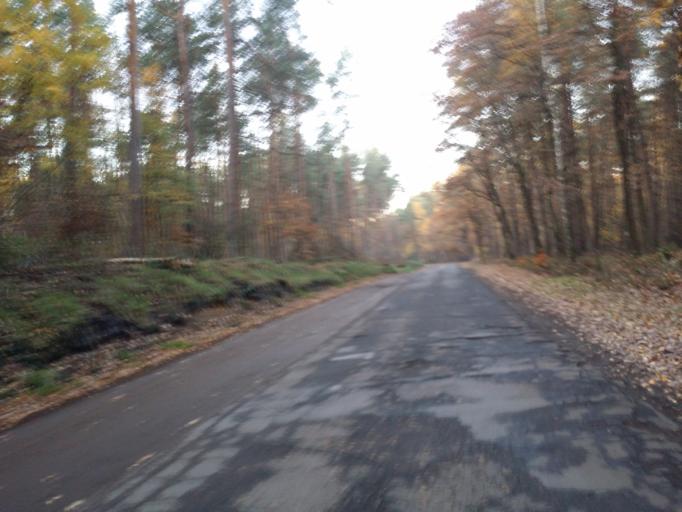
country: DE
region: Lower Saxony
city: Ahausen
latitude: 53.0772
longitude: 9.3060
